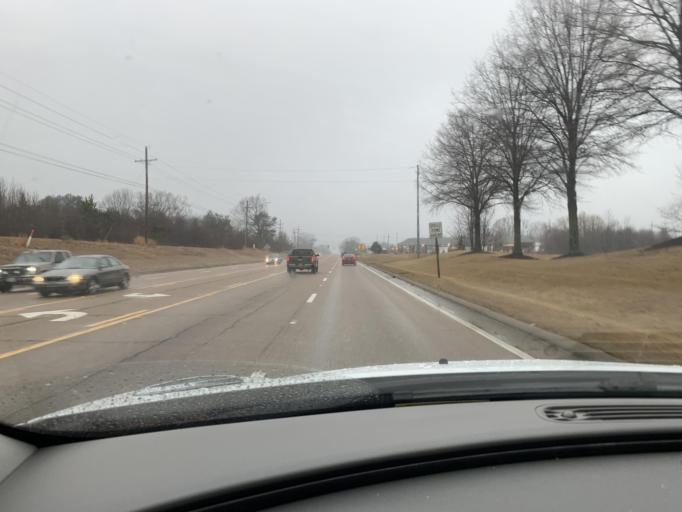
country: US
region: Mississippi
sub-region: De Soto County
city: Horn Lake
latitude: 34.9306
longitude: -90.0122
